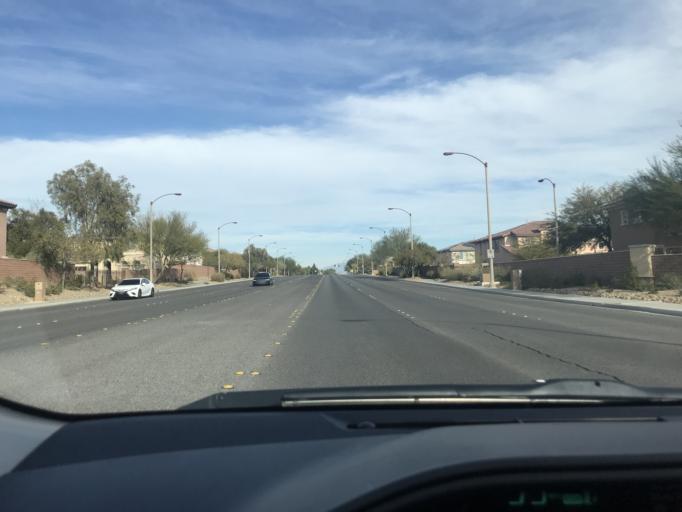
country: US
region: Nevada
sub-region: Clark County
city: Enterprise
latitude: 36.0086
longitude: -115.2799
